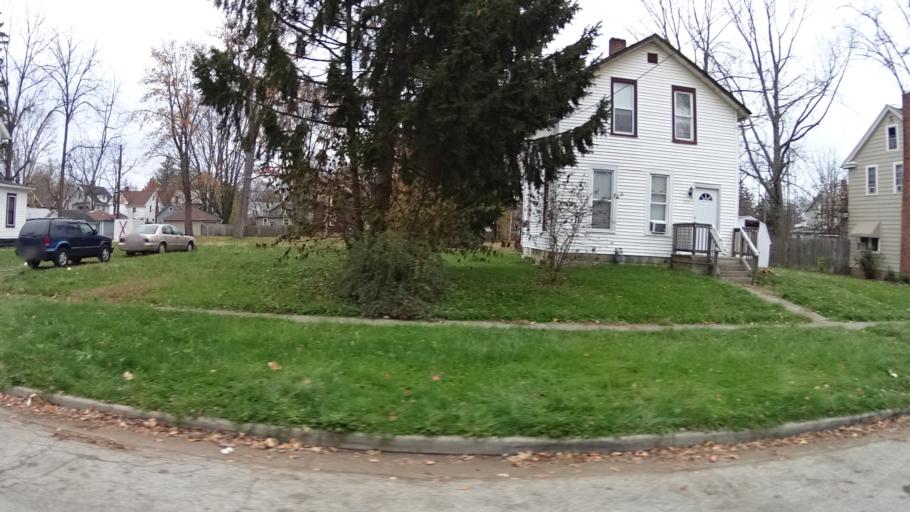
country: US
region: Ohio
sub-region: Lorain County
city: Elyria
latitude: 41.3563
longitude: -82.1083
